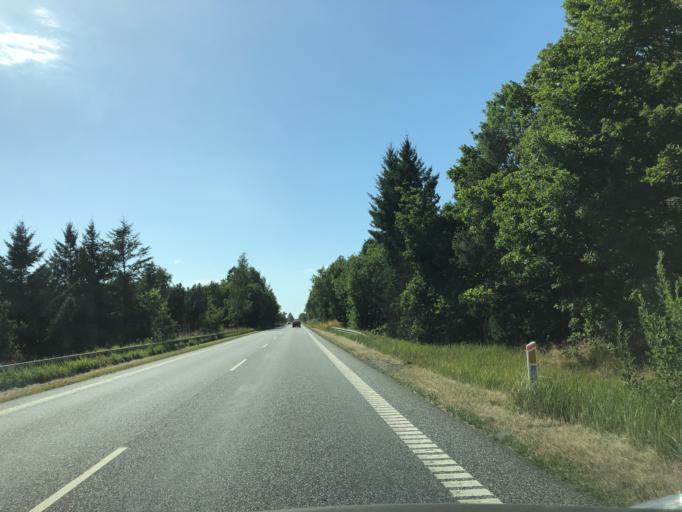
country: DK
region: North Denmark
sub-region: Vesthimmerland Kommune
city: Alestrup
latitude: 56.6116
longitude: 9.4077
